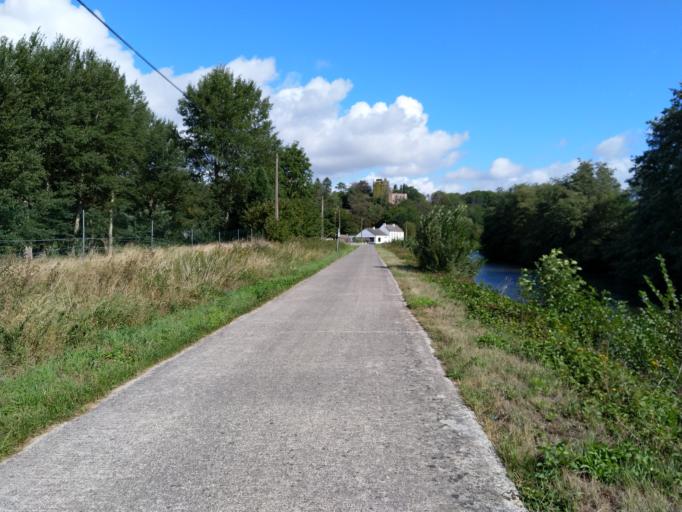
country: BE
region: Wallonia
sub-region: Province du Hainaut
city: Lobbes
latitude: 50.3311
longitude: 4.2305
